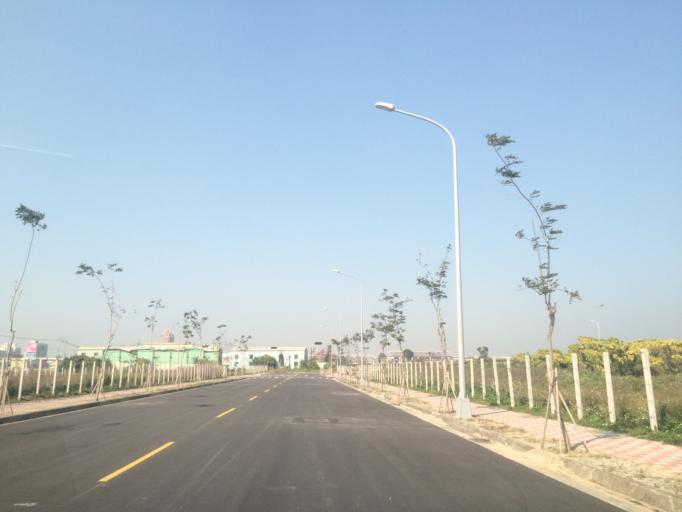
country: TW
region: Taiwan
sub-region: Taichung City
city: Taichung
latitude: 24.1750
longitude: 120.7059
